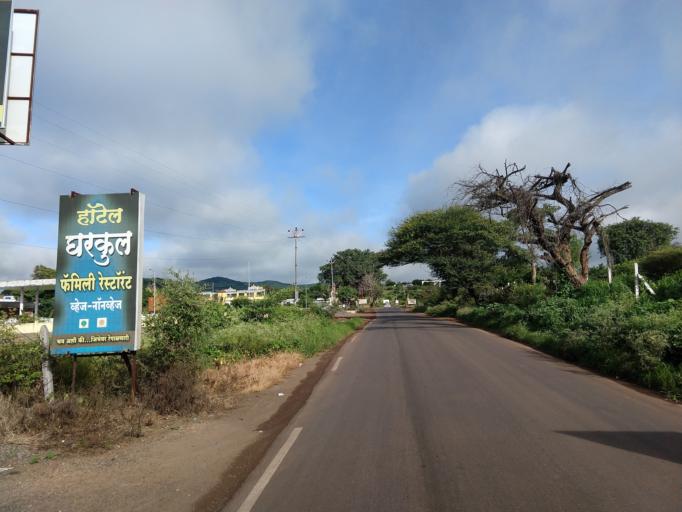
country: IN
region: Maharashtra
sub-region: Pune Division
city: Khed
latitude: 18.3931
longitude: 73.9211
